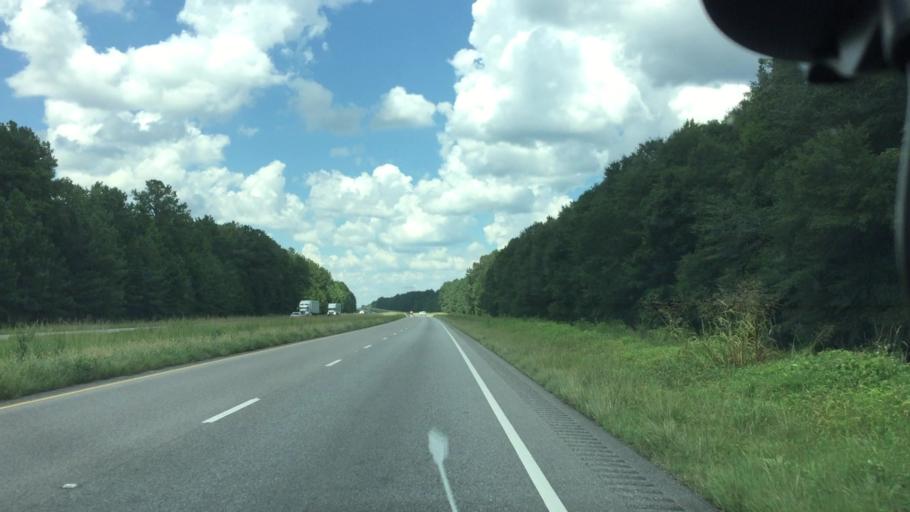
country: US
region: Alabama
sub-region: Pike County
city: Troy
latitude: 31.9924
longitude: -86.0267
